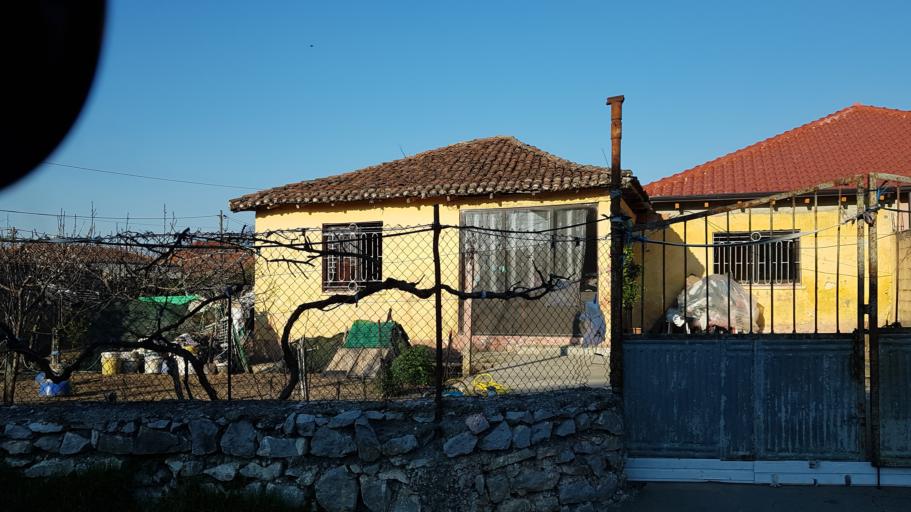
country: AL
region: Shkoder
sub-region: Rrethi i Shkodres
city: Shkoder
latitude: 42.0779
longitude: 19.5016
